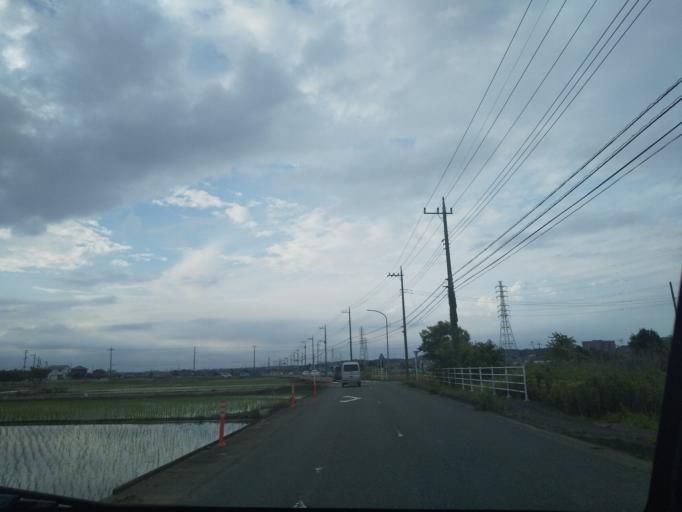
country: JP
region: Kanagawa
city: Zama
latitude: 35.4878
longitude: 139.3855
